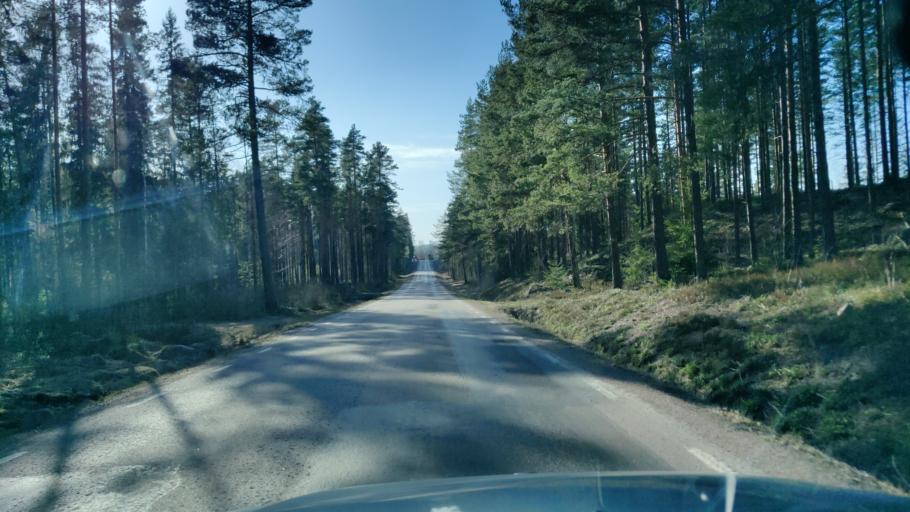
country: SE
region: Vaermland
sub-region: Sunne Kommun
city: Sunne
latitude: 59.9927
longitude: 13.3032
